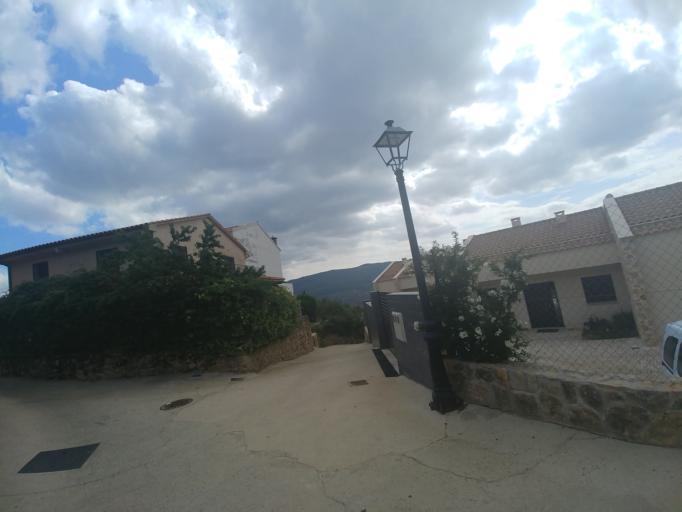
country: ES
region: Extremadura
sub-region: Provincia de Caceres
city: Casas del Castanar
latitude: 40.1346
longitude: -5.9475
